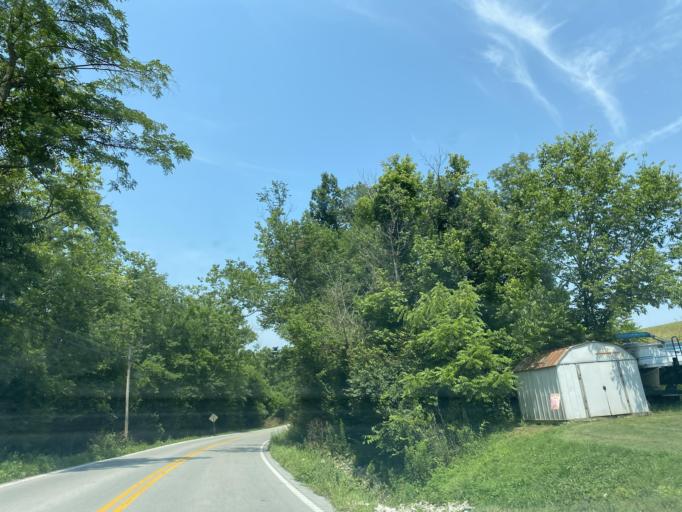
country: US
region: Kentucky
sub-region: Kenton County
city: Ryland Heights
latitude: 38.9081
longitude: -84.4495
